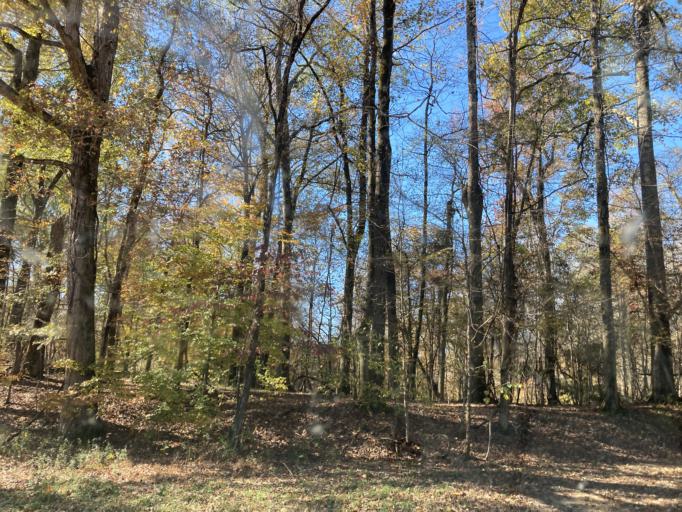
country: US
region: Mississippi
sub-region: Hinds County
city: Lynchburg
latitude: 32.5698
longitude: -90.5108
